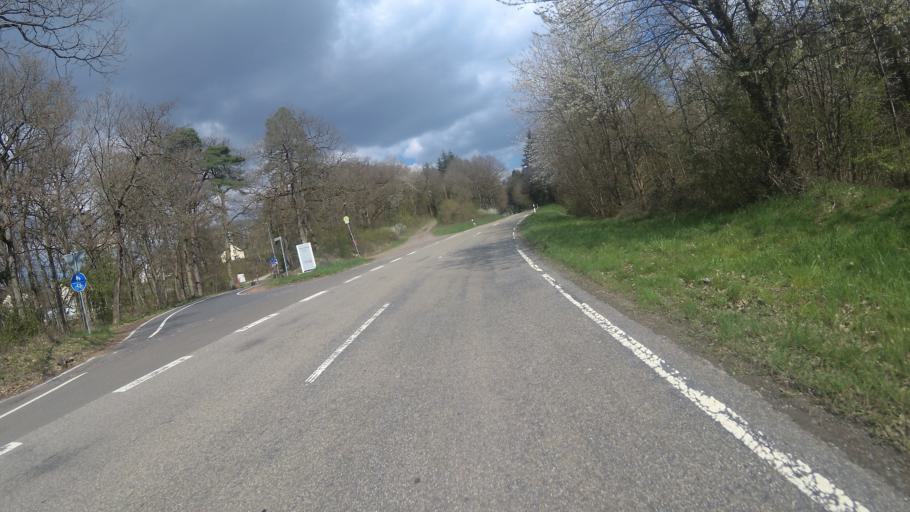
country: DE
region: Rheinland-Pfalz
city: Wittlich
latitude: 50.0071
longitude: 6.8977
